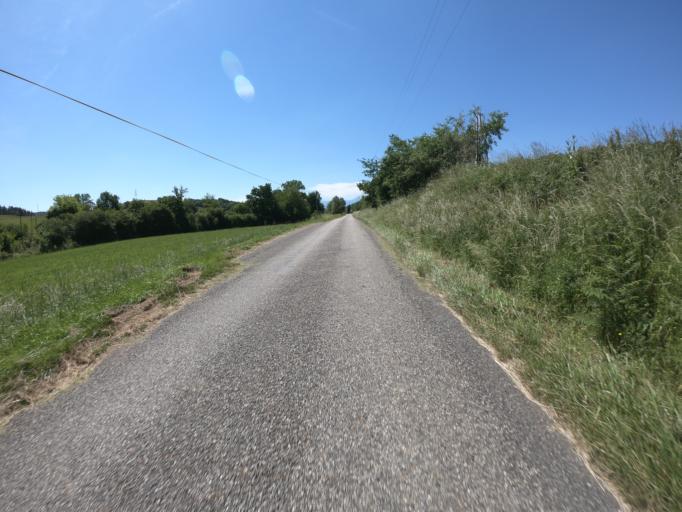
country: FR
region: Languedoc-Roussillon
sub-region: Departement de l'Aude
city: Belpech
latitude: 43.1221
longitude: 1.7720
